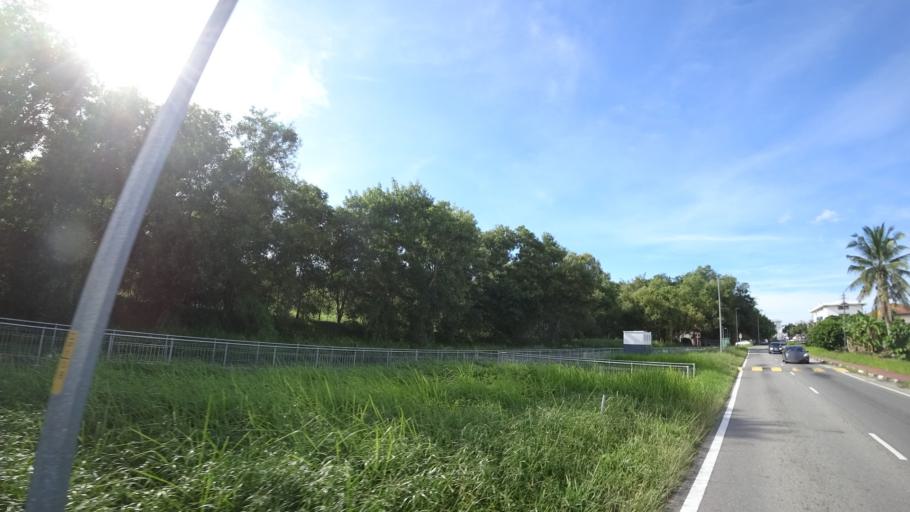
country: BN
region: Brunei and Muara
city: Bandar Seri Begawan
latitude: 4.9139
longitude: 114.9131
